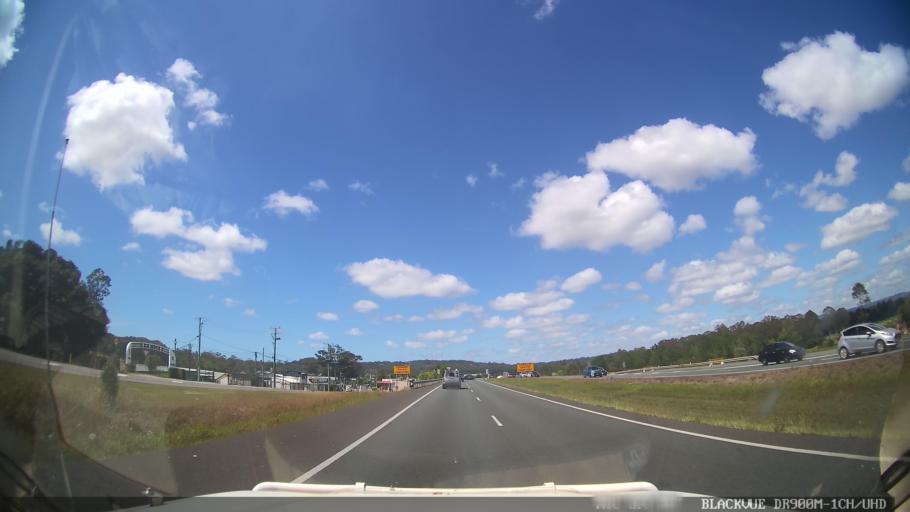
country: AU
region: Queensland
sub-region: Sunshine Coast
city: Woombye
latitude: -26.6843
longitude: 153.0032
